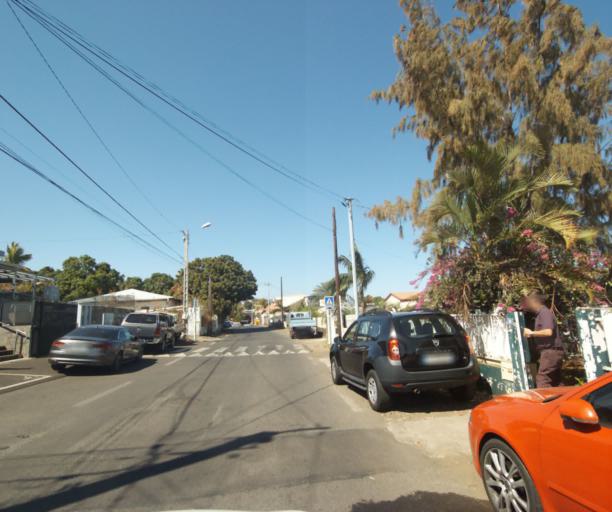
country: RE
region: Reunion
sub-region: Reunion
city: La Possession
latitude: -20.9813
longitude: 55.3274
